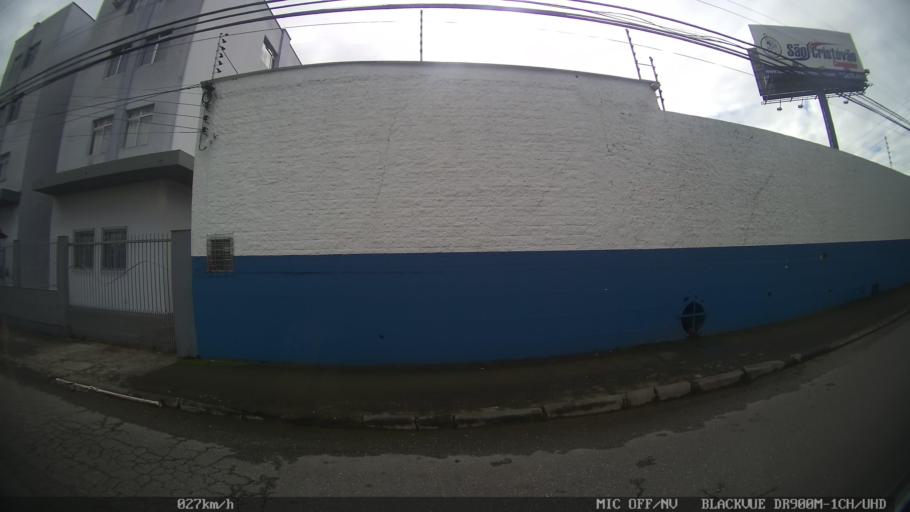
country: BR
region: Santa Catarina
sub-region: Sao Jose
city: Campinas
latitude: -27.5478
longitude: -48.6206
